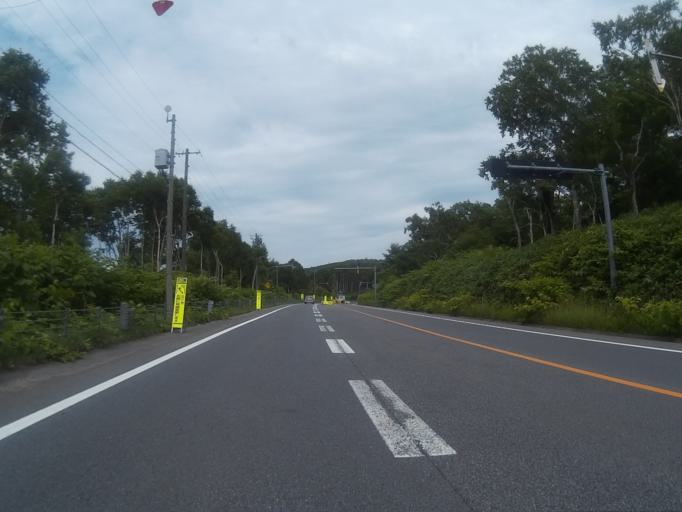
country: JP
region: Hokkaido
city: Sapporo
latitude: 42.8484
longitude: 141.0832
